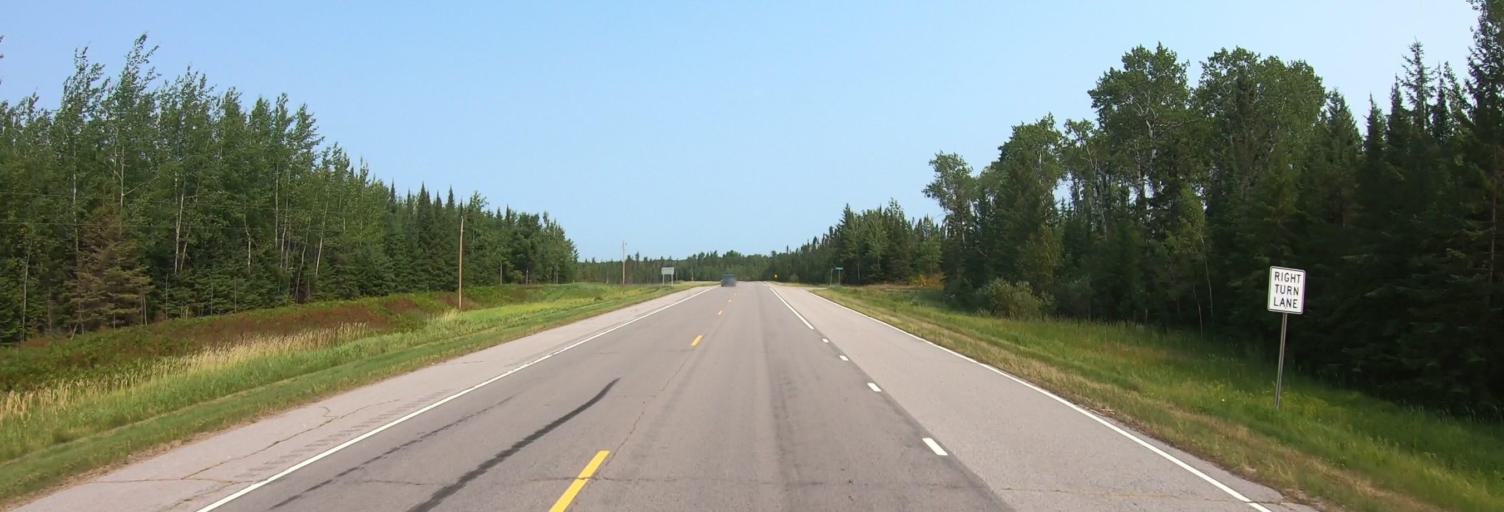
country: US
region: Minnesota
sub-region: Saint Louis County
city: Mountain Iron
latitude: 48.0825
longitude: -92.8223
